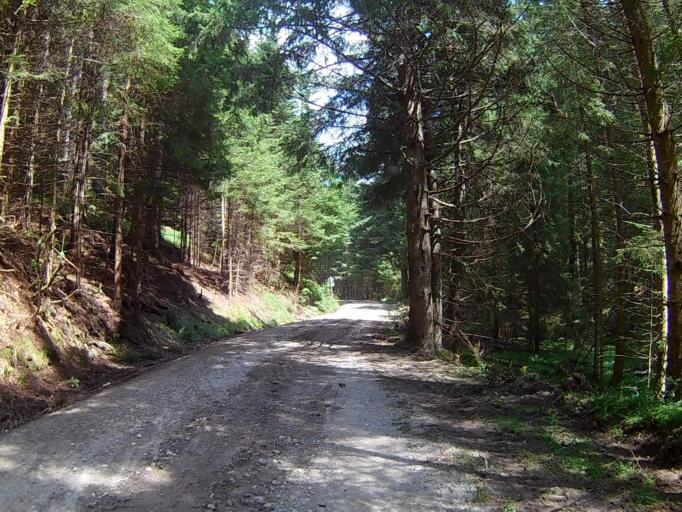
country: SI
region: Lovrenc na Pohorju
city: Lovrenc na Pohorju
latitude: 46.4803
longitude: 15.4299
